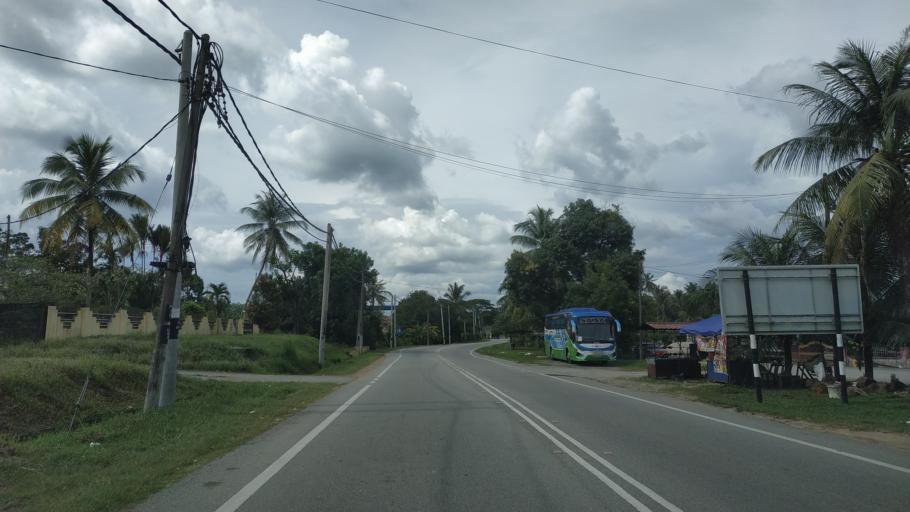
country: MY
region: Kedah
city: Kulim
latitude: 5.4236
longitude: 100.6645
